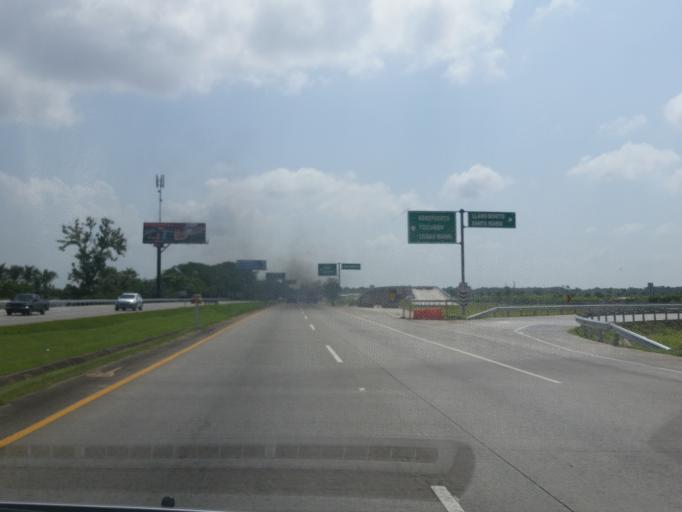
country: PA
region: Panama
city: San Miguelito
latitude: 9.0295
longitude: -79.4545
